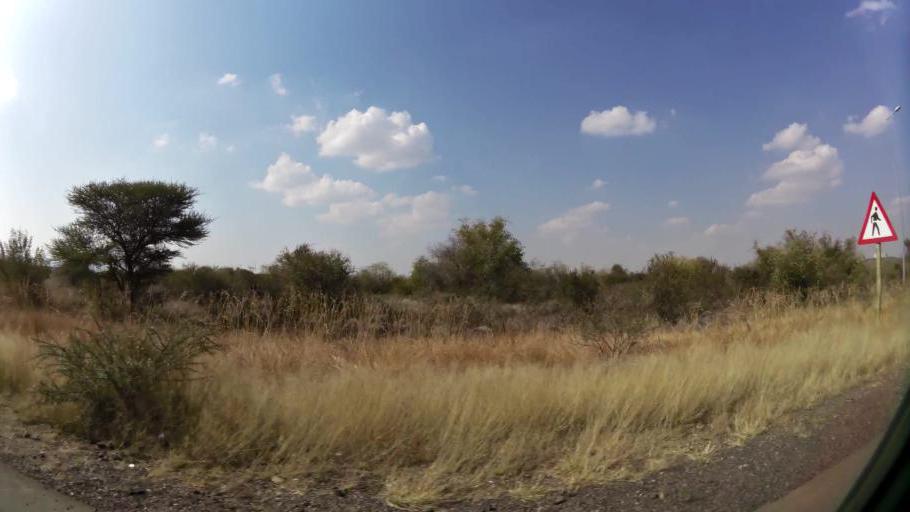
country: ZA
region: North-West
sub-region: Bojanala Platinum District Municipality
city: Mogwase
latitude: -25.4186
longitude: 27.0786
